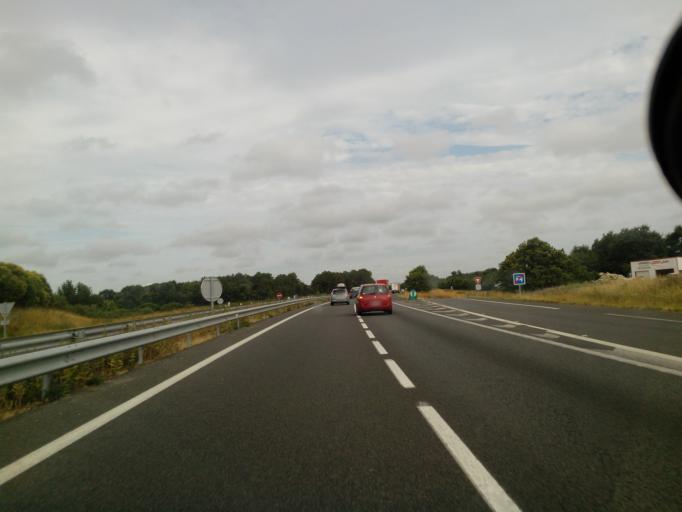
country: FR
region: Brittany
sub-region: Departement du Morbihan
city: Marzan
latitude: 47.5303
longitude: -2.3271
